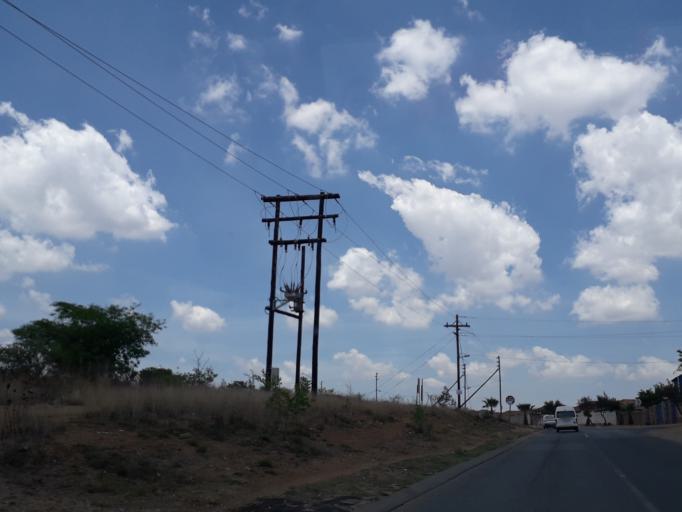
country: ZA
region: Gauteng
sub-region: West Rand District Municipality
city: Muldersdriseloop
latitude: -26.0418
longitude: 27.9228
